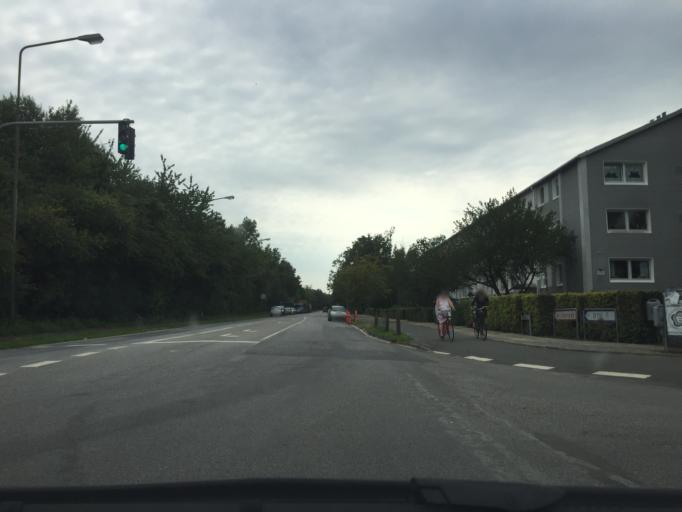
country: DK
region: Capital Region
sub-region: Lyngby-Tarbaek Kommune
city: Kongens Lyngby
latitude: 55.7953
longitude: 12.5295
